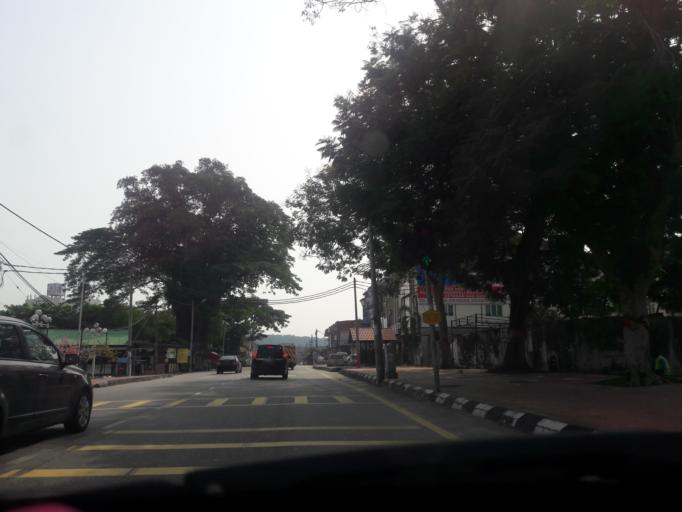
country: MY
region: Kedah
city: Kulim
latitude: 5.3687
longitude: 100.5538
